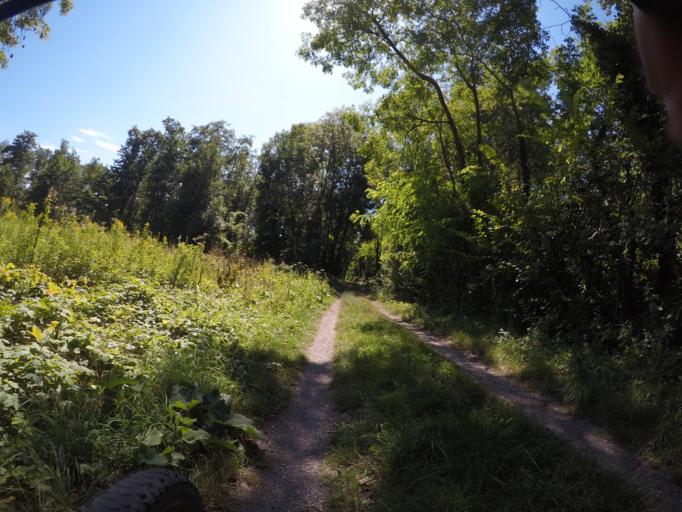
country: AT
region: Lower Austria
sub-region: Politischer Bezirk Wien-Umgebung
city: Moosbrunn
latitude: 48.0125
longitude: 16.4477
